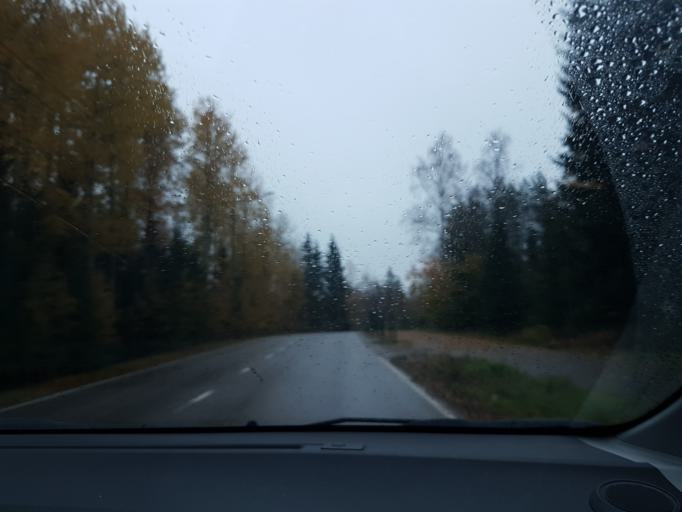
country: FI
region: Uusimaa
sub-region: Helsinki
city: Jaervenpaeae
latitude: 60.5651
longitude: 25.1373
